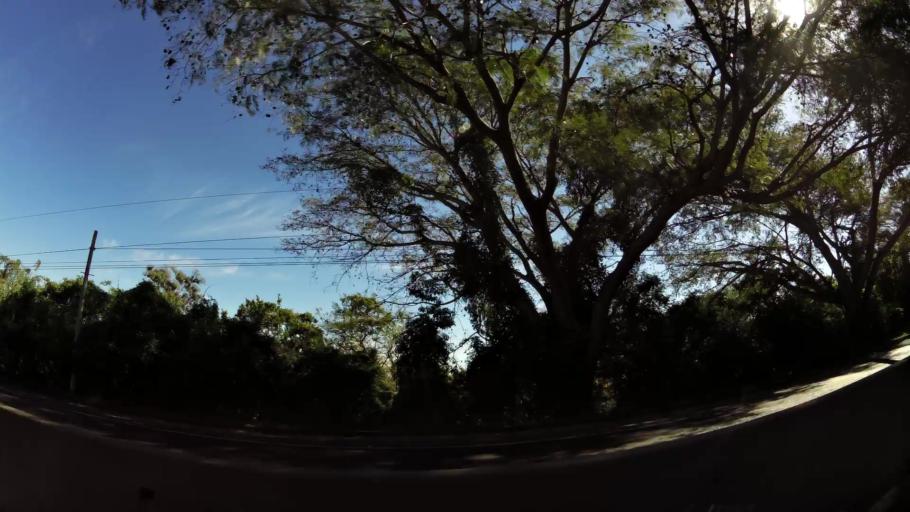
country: SV
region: Santa Ana
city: Coatepeque
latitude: 13.9219
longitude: -89.5188
